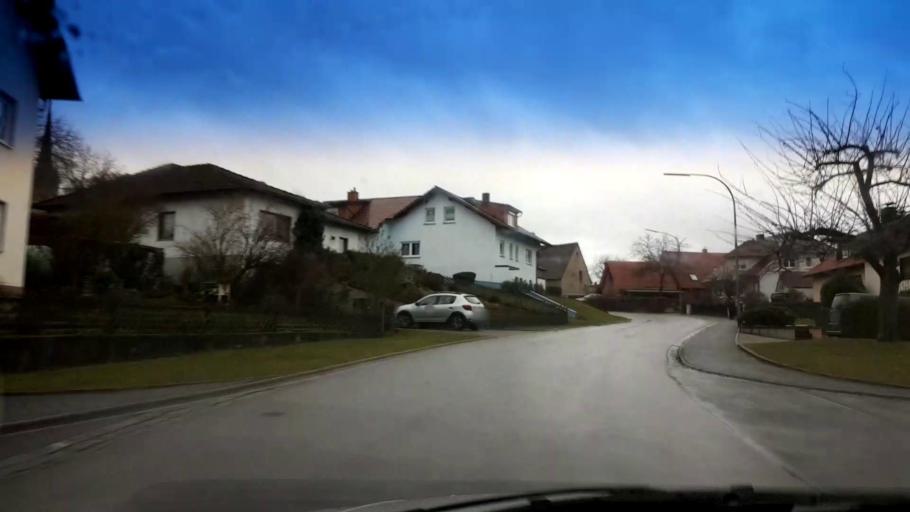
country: DE
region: Bavaria
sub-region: Upper Franconia
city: Litzendorf
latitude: 49.8726
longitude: 11.0448
